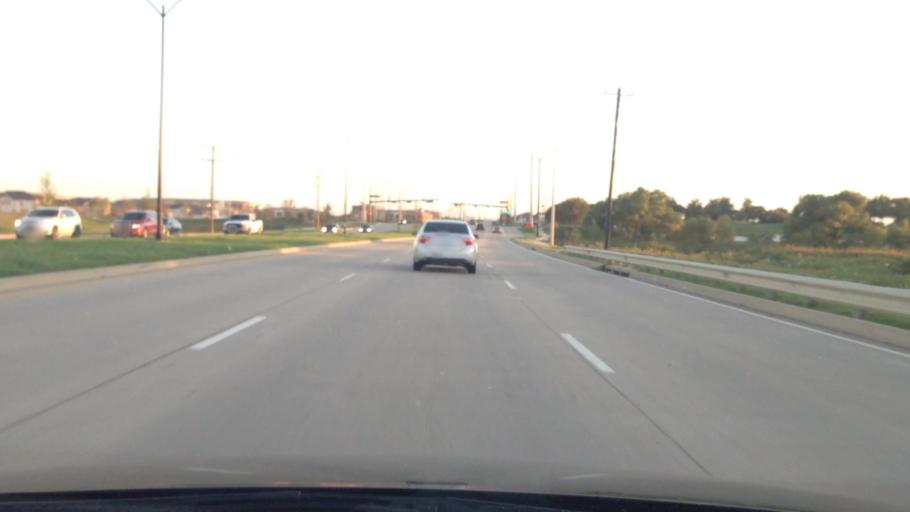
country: US
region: Texas
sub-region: Denton County
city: The Colony
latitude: 33.1389
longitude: -96.8907
